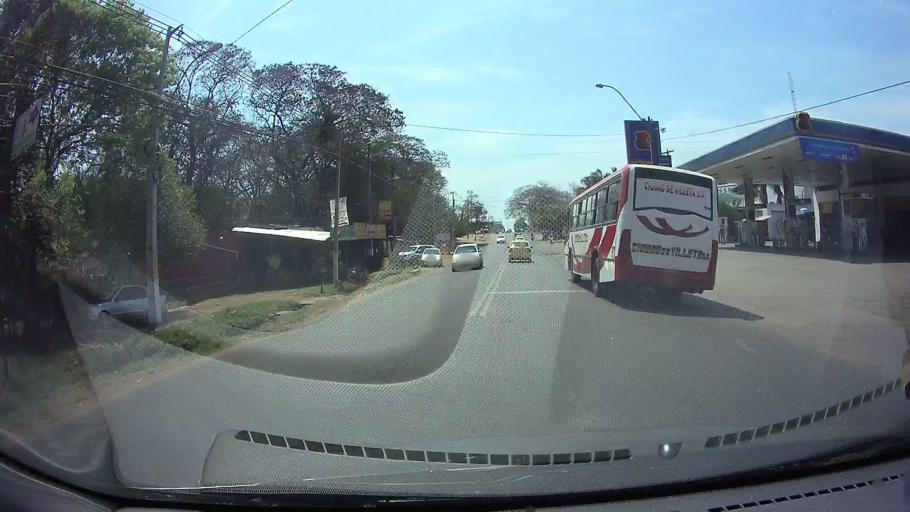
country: PY
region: Central
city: Capiata
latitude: -25.3792
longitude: -57.4751
